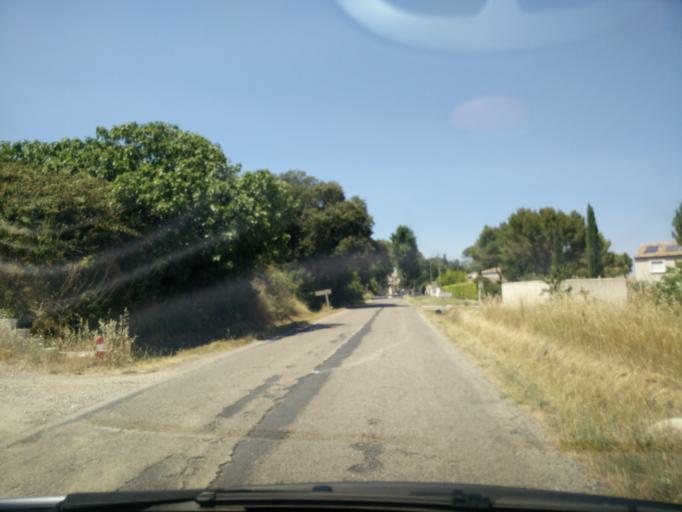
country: FR
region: Languedoc-Roussillon
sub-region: Departement de l'Herault
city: Saint-Christol
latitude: 43.7279
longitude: 4.1077
